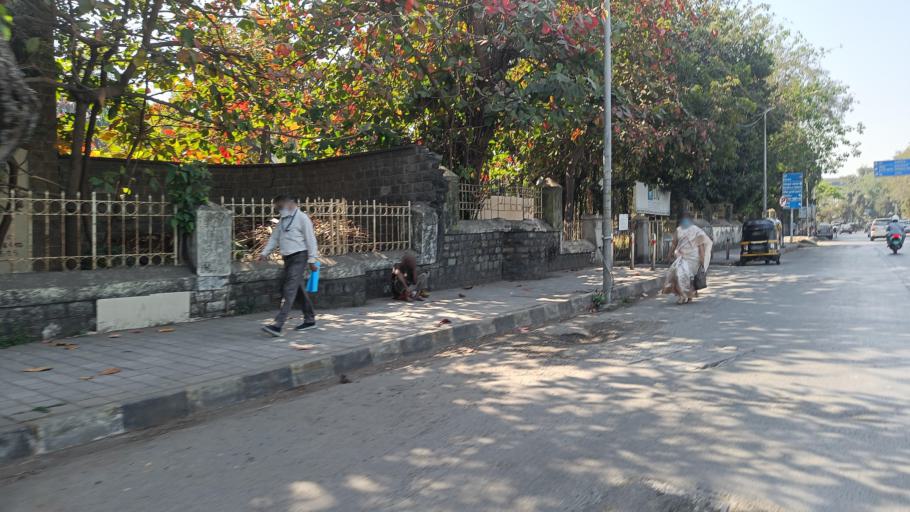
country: IN
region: Maharashtra
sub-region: Mumbai Suburban
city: Mumbai
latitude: 19.0927
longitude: 72.8392
